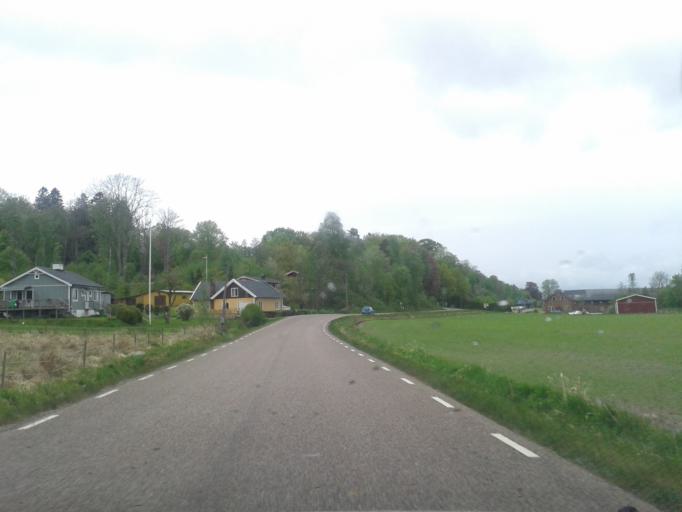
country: SE
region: Vaestra Goetaland
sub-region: Lilla Edets Kommun
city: Lodose
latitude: 58.0304
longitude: 12.1378
